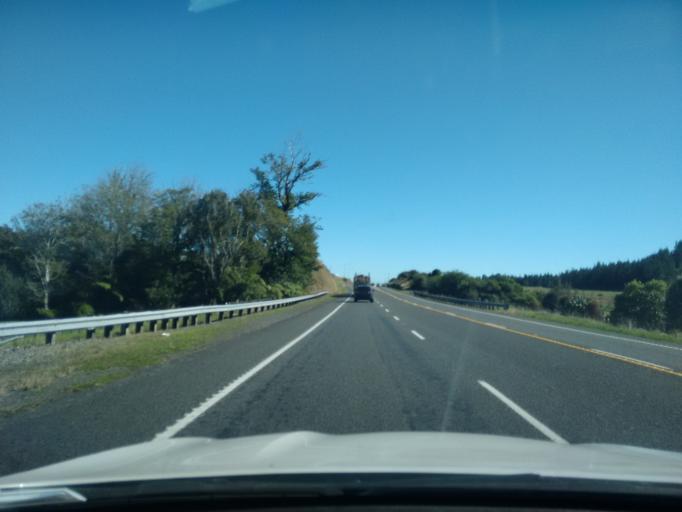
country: NZ
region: Taranaki
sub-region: New Plymouth District
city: New Plymouth
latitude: -39.1376
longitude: 174.1311
